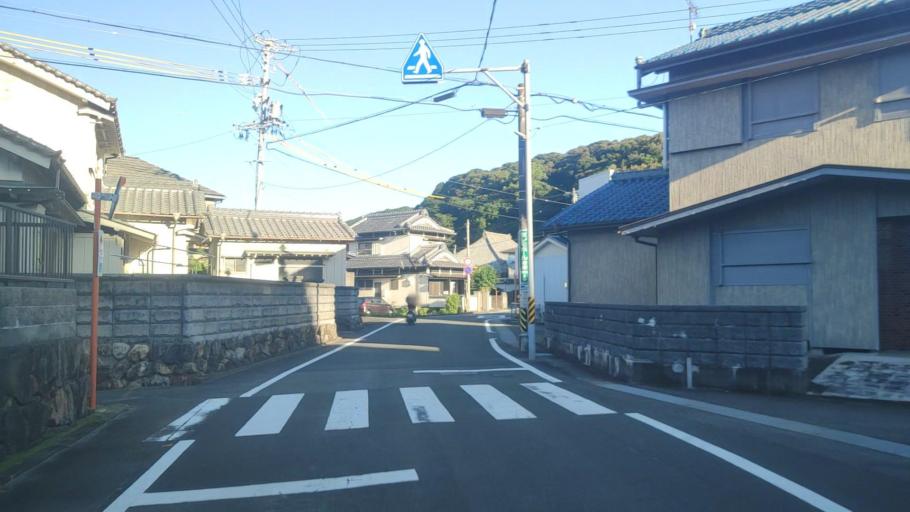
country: JP
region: Mie
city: Ise
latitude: 34.2764
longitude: 136.7684
